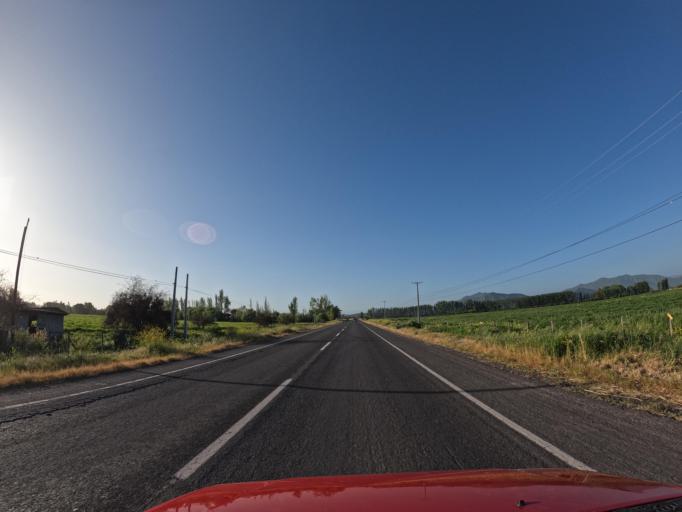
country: CL
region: O'Higgins
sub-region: Provincia de Colchagua
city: Santa Cruz
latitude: -34.4629
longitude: -71.3633
